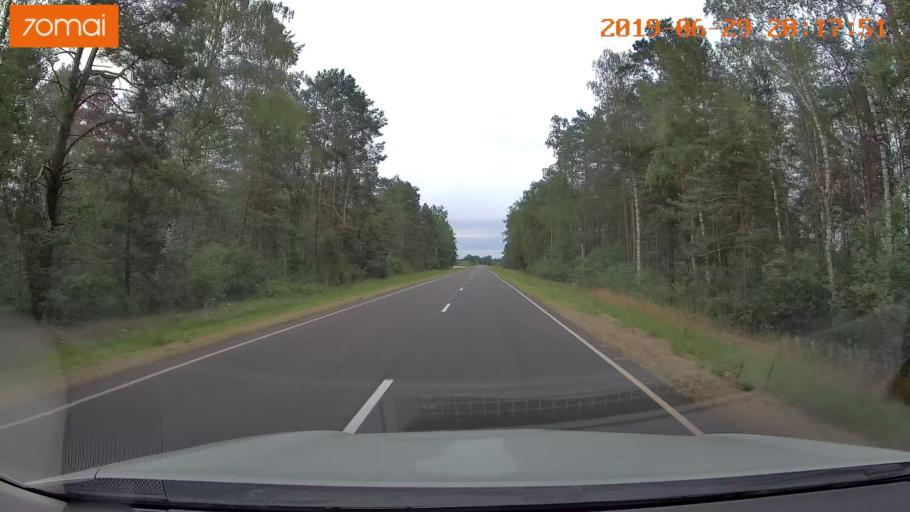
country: BY
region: Brest
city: Asnyezhytsy
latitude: 52.3909
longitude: 26.2246
